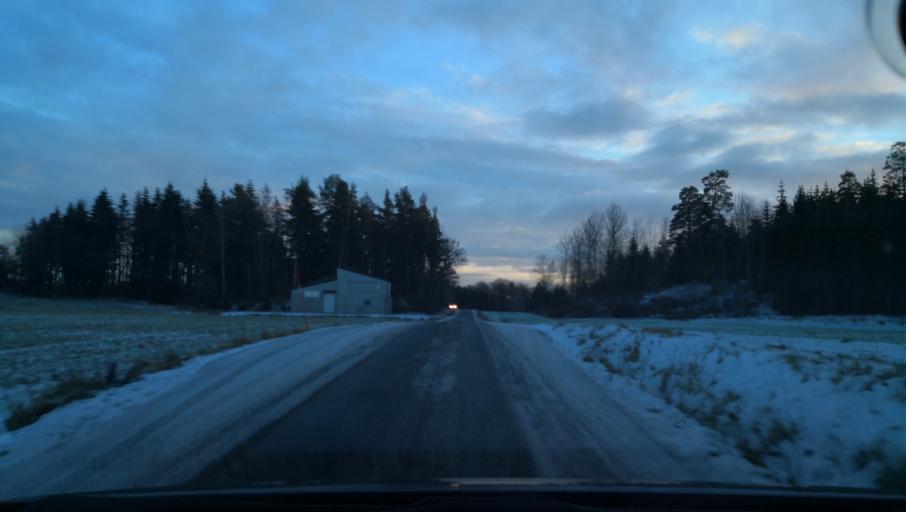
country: SE
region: Soedermanland
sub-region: Eskilstuna Kommun
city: Skogstorp
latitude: 59.2301
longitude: 16.3352
